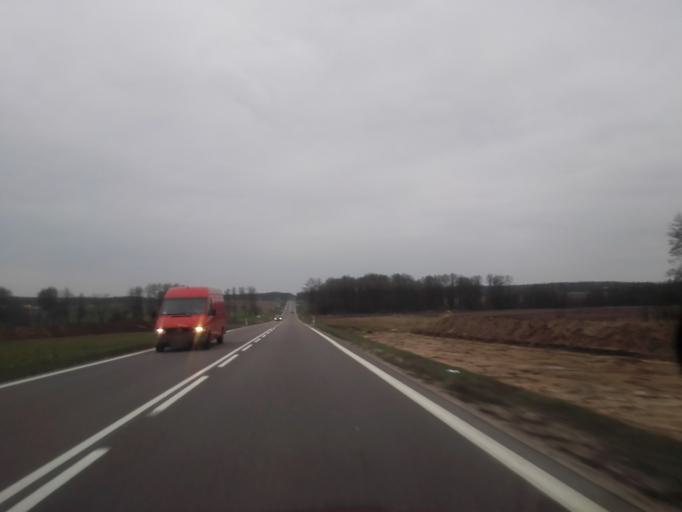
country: PL
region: Podlasie
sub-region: Powiat grajewski
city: Szczuczyn
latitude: 53.5369
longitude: 22.2627
